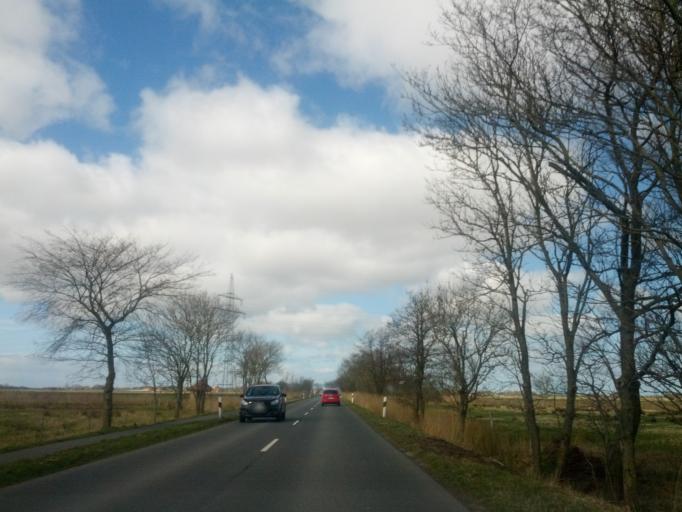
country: DE
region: Lower Saxony
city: Esens
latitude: 53.6635
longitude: 7.6002
